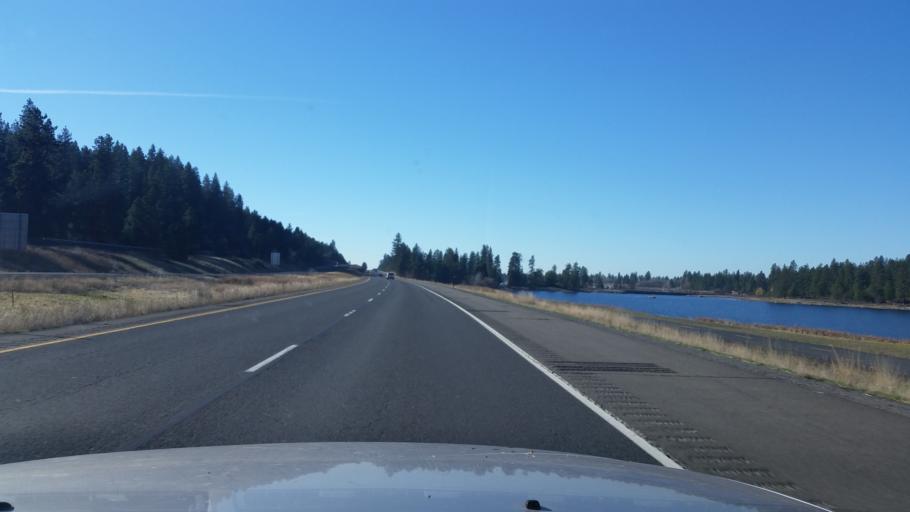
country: US
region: Washington
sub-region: Spokane County
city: Medical Lake
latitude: 47.5573
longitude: -117.6132
